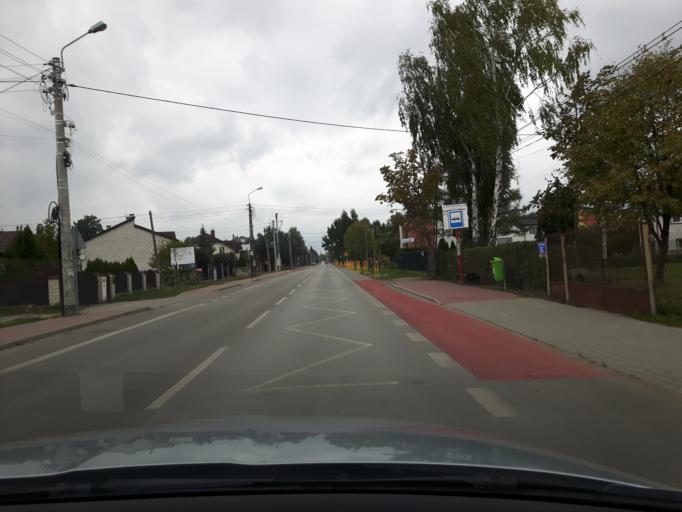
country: PL
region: Masovian Voivodeship
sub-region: Powiat wolominski
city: Kobylka
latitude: 52.3212
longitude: 21.1897
